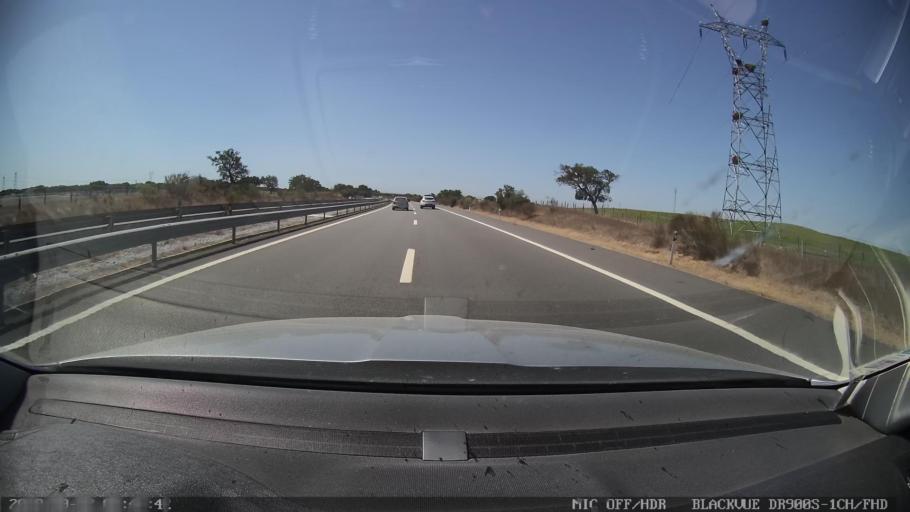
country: PT
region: Setubal
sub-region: Palmela
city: Palmela
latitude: 38.5999
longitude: -8.7409
